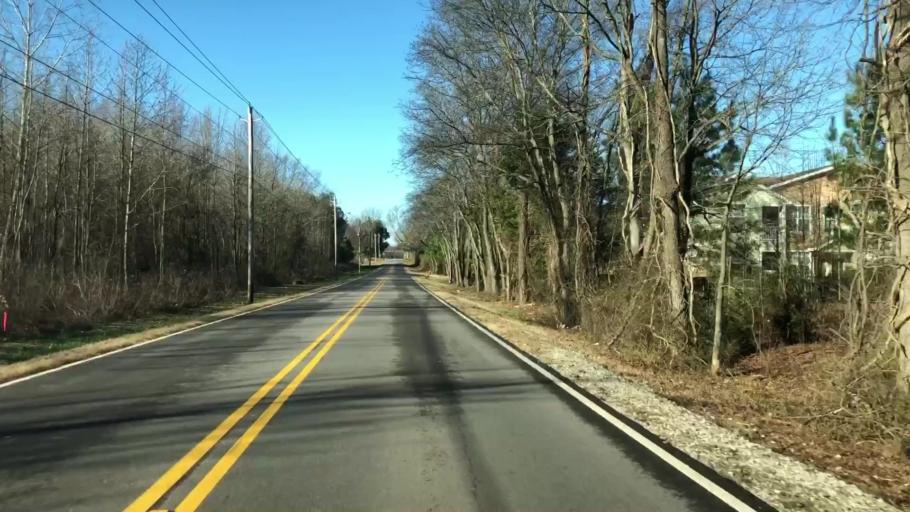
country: US
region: Alabama
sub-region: Madison County
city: Madison
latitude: 34.6923
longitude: -86.7802
